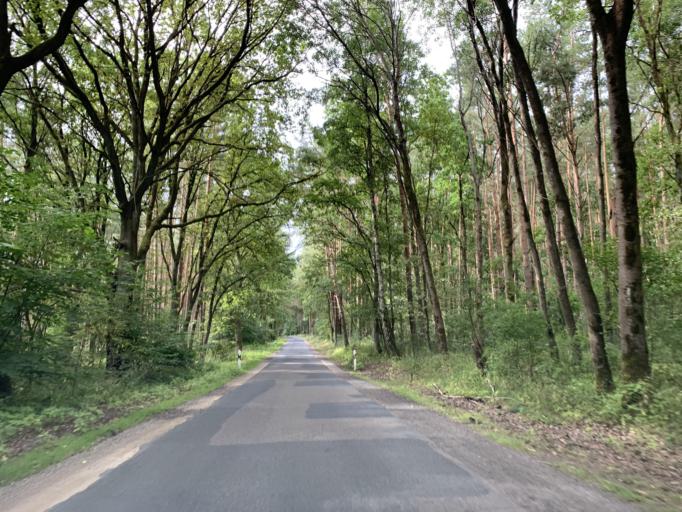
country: DE
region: Mecklenburg-Vorpommern
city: Blankensee
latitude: 53.3979
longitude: 13.2619
